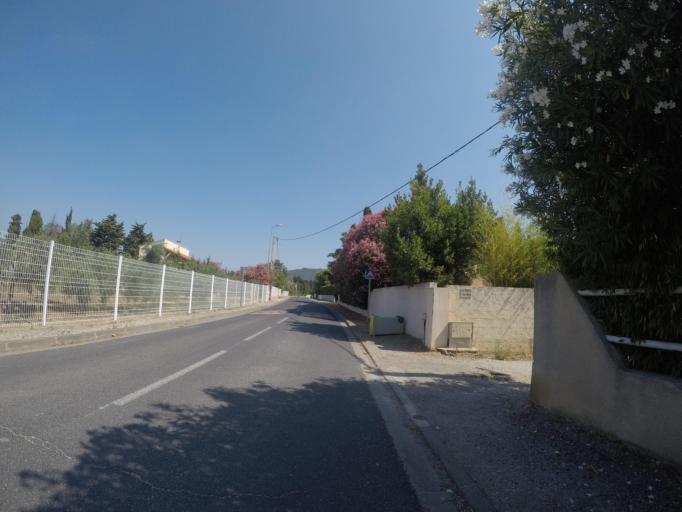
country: FR
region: Languedoc-Roussillon
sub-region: Departement des Pyrenees-Orientales
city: Millas
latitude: 42.6864
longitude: 2.6910
